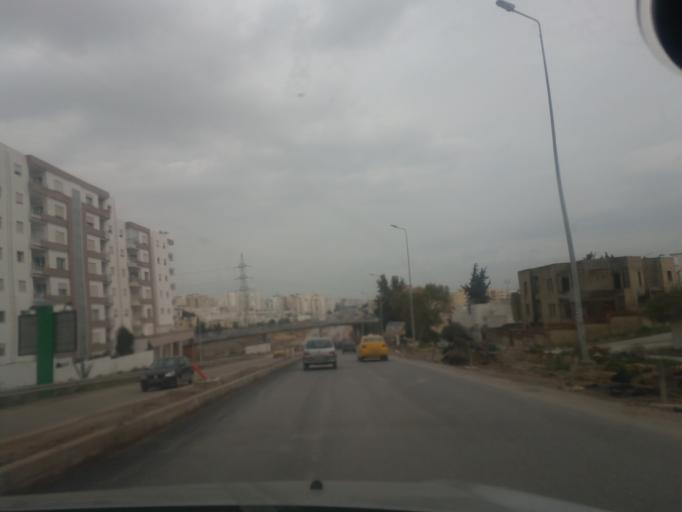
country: TN
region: Tunis
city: Tunis
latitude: 36.8548
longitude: 10.1437
